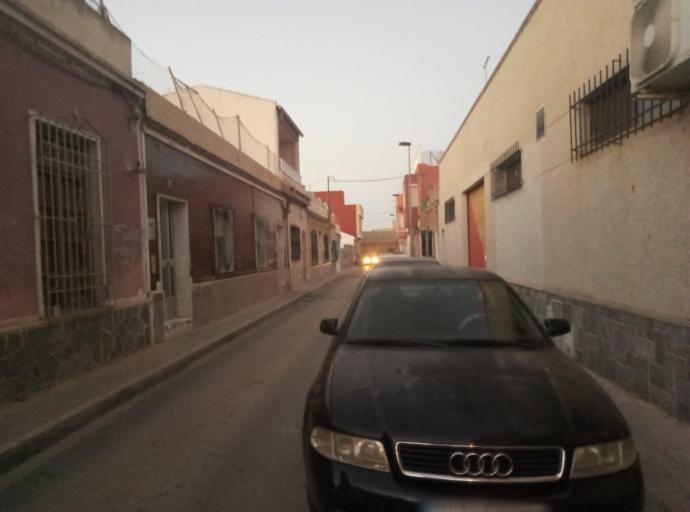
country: ES
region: Murcia
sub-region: Murcia
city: Cartagena
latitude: 37.6380
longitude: -1.0115
